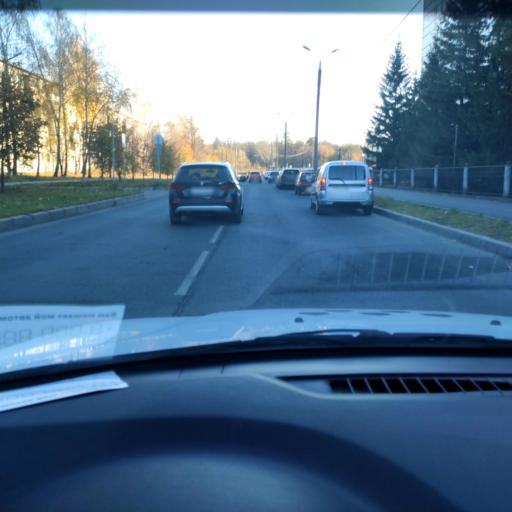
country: RU
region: Samara
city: Tol'yatti
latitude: 53.5006
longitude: 49.4013
